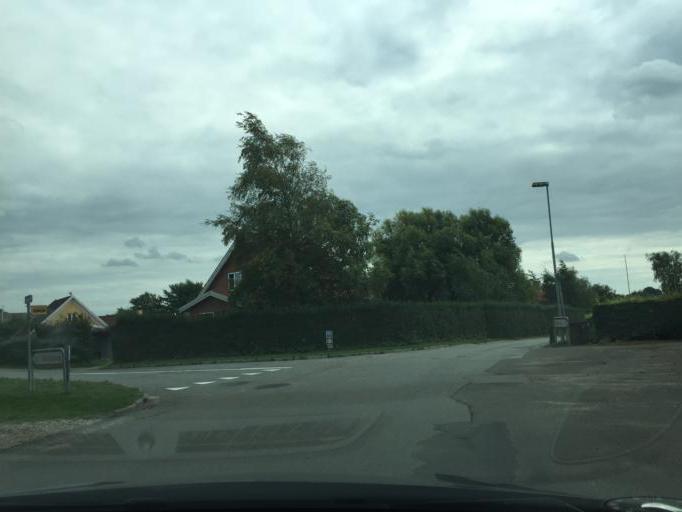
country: DK
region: South Denmark
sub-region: Assens Kommune
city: Vissenbjerg
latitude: 55.3484
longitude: 10.0936
